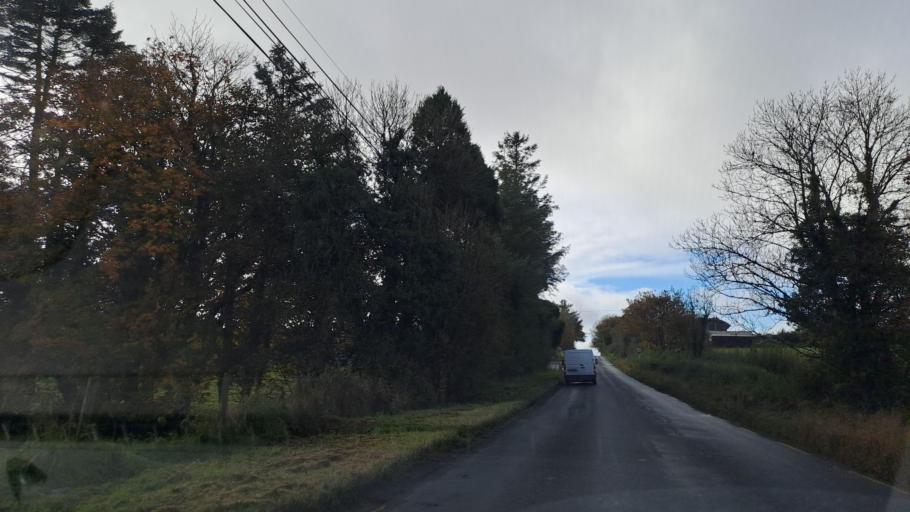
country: IE
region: Ulster
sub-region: An Cabhan
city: Virginia
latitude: 53.8448
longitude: -7.0674
